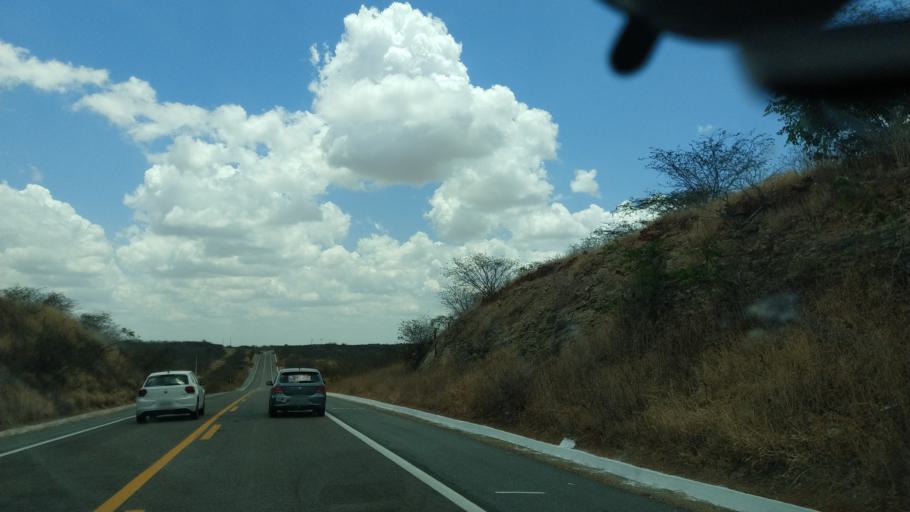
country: BR
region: Rio Grande do Norte
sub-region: Cerro Cora
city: Cerro Cora
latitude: -6.2013
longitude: -36.2734
